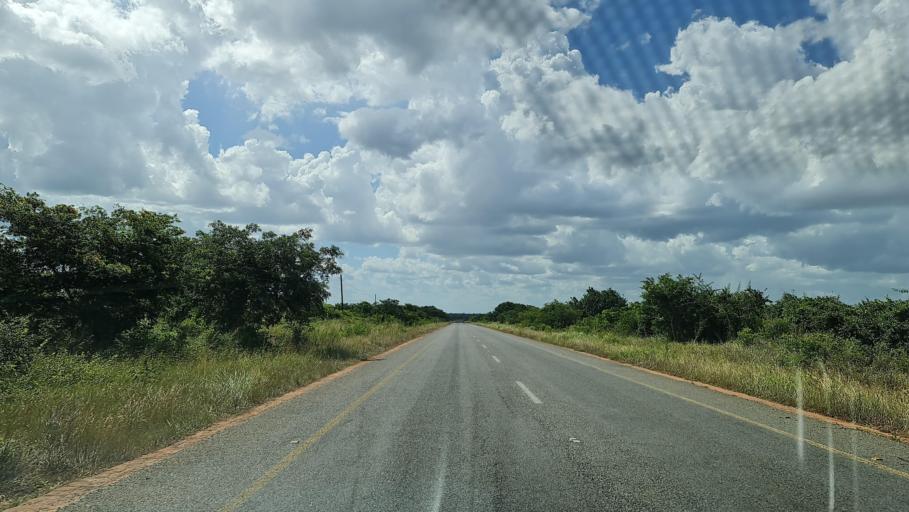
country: MZ
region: Inhambane
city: Maxixe
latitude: -22.9686
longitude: 35.2159
